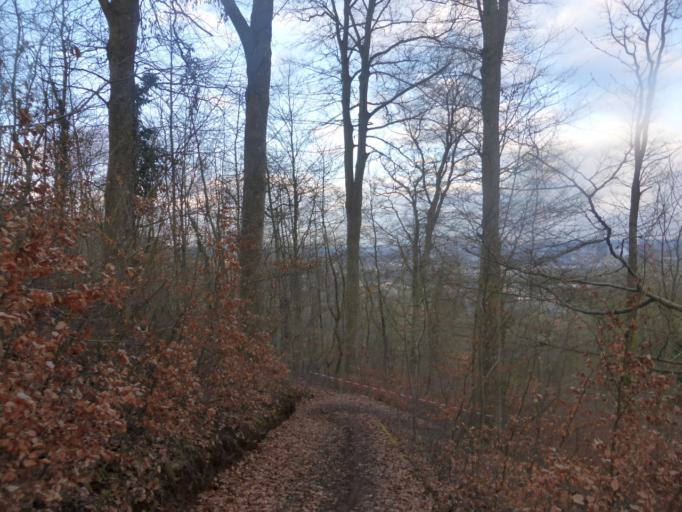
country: LU
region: Luxembourg
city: Belvaux
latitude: 49.5078
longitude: 5.9175
